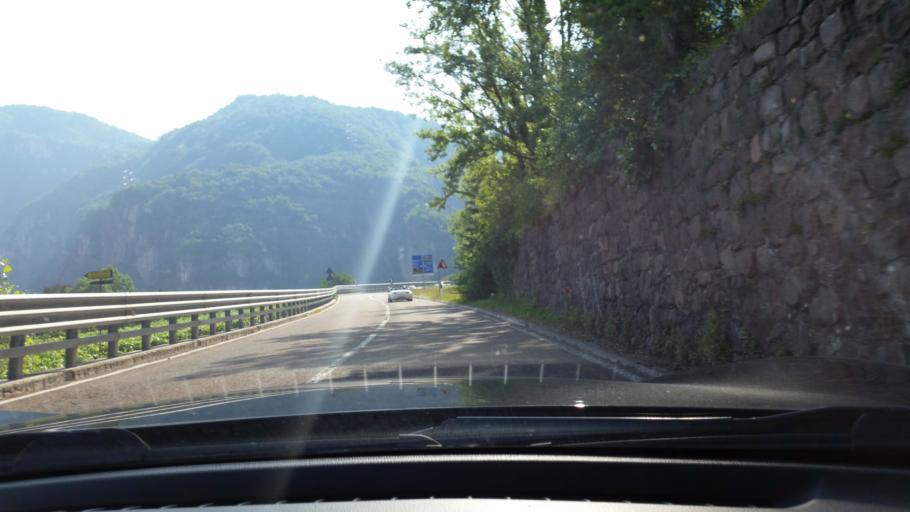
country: IT
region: Trentino-Alto Adige
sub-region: Bolzano
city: Ora
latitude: 46.3433
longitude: 11.2983
